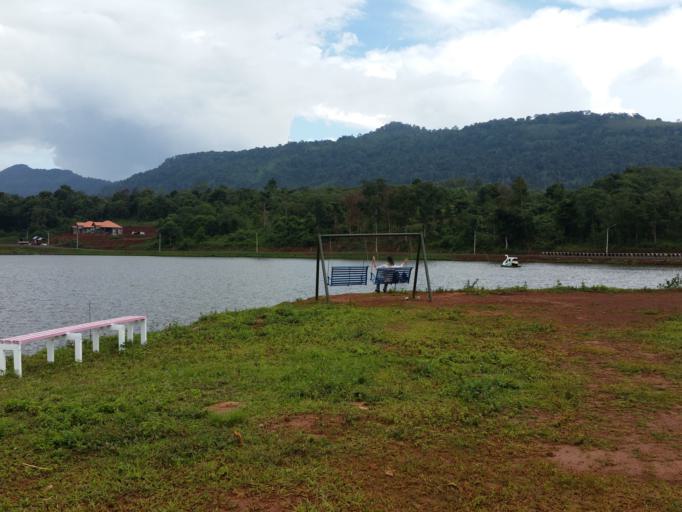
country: LA
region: Xekong
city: Thateng
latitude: 15.3890
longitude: 106.3761
